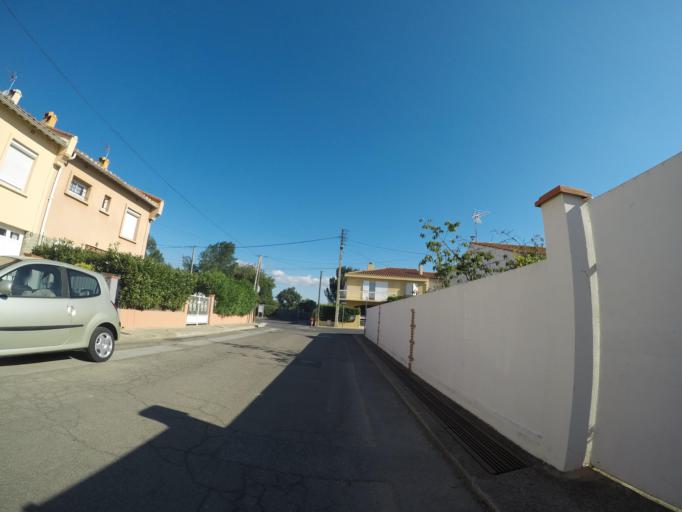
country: FR
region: Languedoc-Roussillon
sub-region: Departement des Pyrenees-Orientales
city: Le Soler
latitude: 42.6824
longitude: 2.7899
